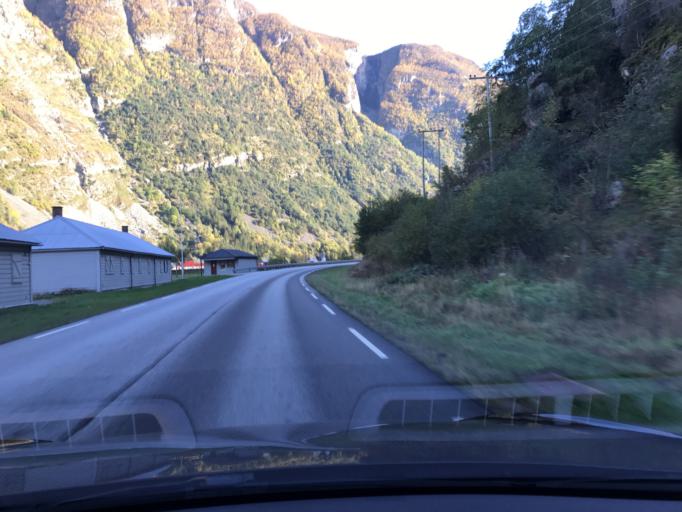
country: NO
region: Sogn og Fjordane
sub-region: Laerdal
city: Laerdalsoyri
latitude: 61.0980
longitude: 7.5157
